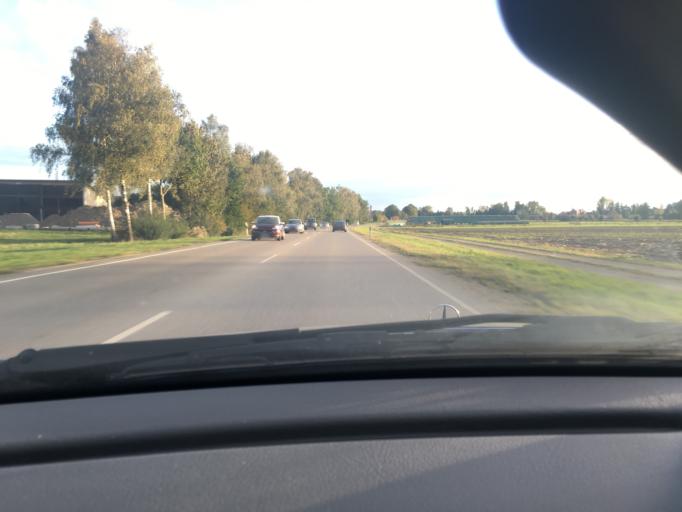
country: DE
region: Bavaria
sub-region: Swabia
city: Gablingen
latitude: 48.4256
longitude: 10.8268
